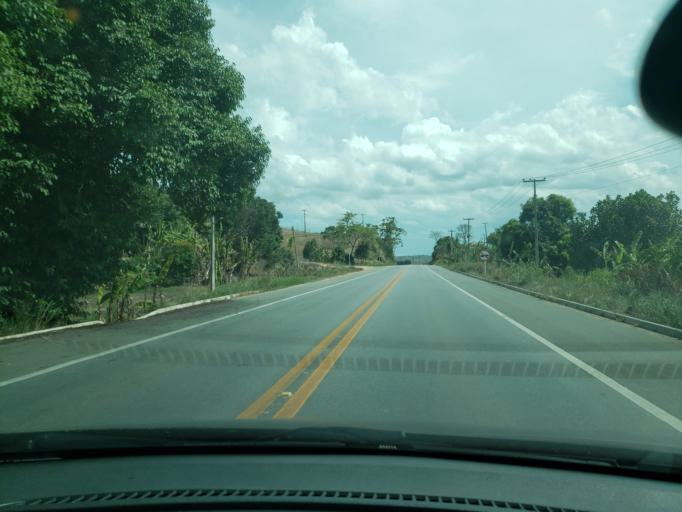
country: BR
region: Alagoas
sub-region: Murici
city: Murici
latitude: -9.2839
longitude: -35.9625
